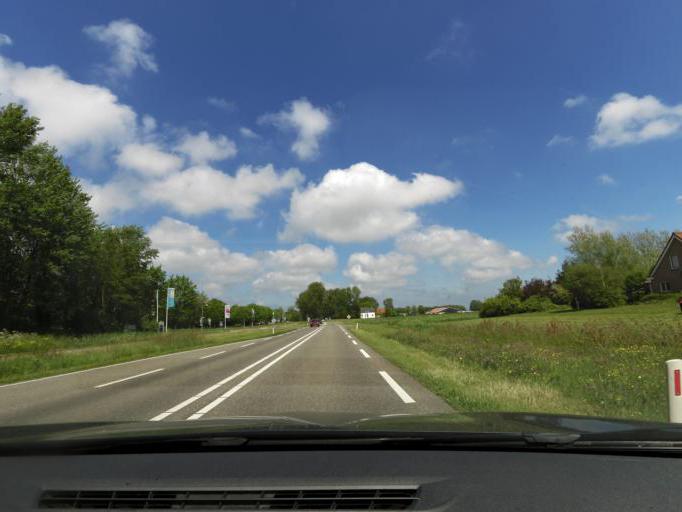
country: NL
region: Zeeland
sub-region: Schouwen-Duiveland
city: Burgh
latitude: 51.6840
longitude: 3.7312
